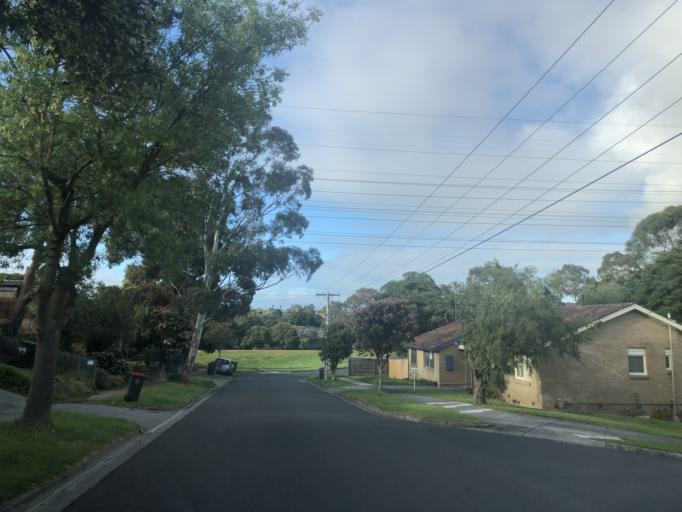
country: AU
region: Victoria
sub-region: Monash
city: Notting Hill
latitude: -37.8882
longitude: 145.1230
